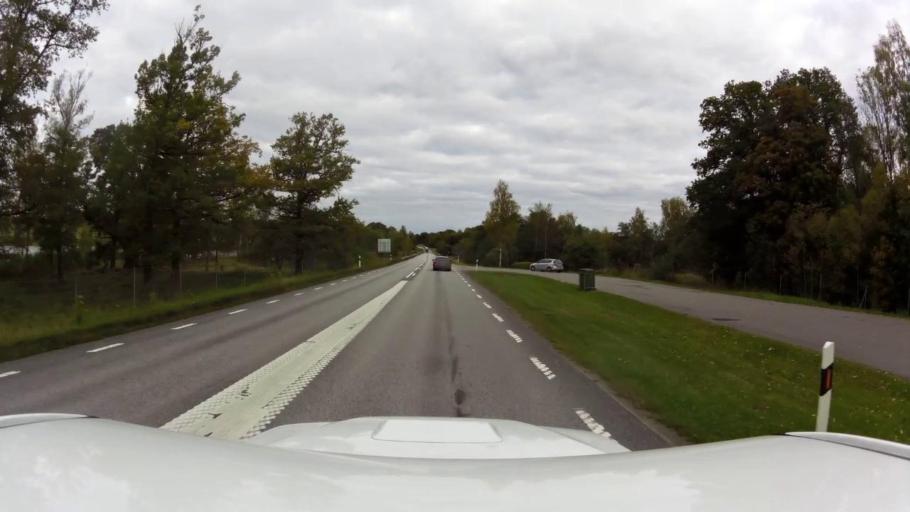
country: SE
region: OEstergoetland
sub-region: Kinda Kommun
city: Rimforsa
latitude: 58.2141
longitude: 15.6670
